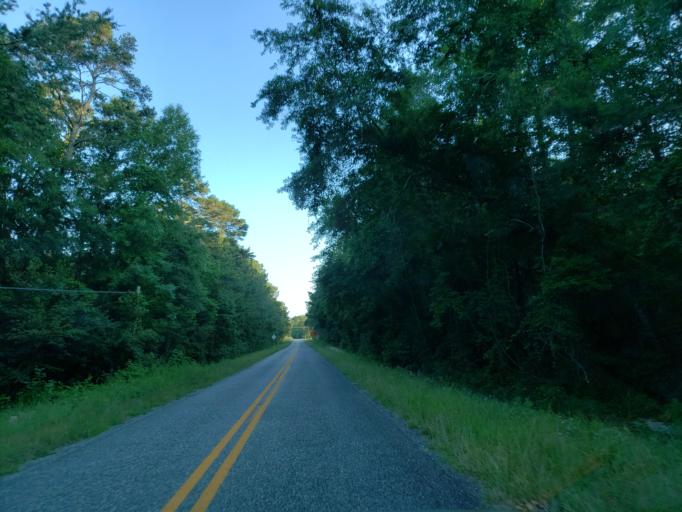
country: US
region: Georgia
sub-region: Crisp County
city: Cordele
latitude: 32.0088
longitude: -83.7546
